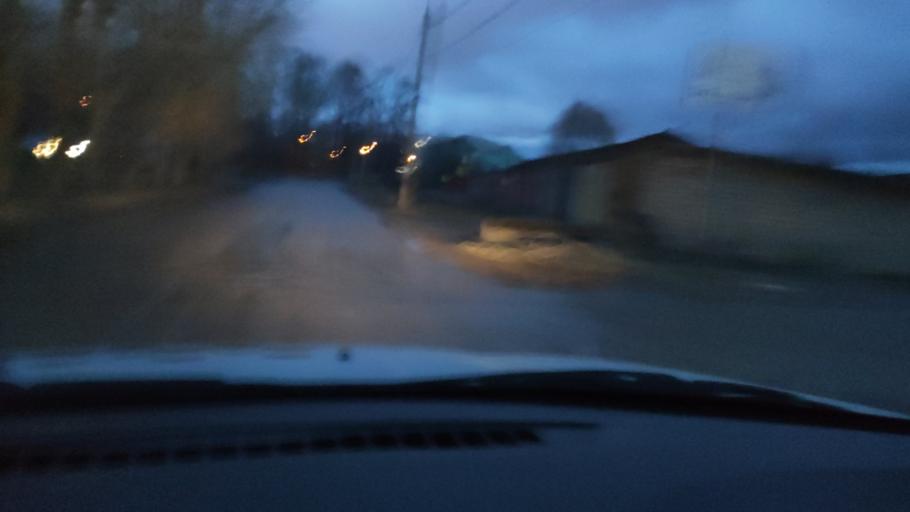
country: RU
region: Perm
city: Perm
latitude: 57.9736
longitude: 56.2784
